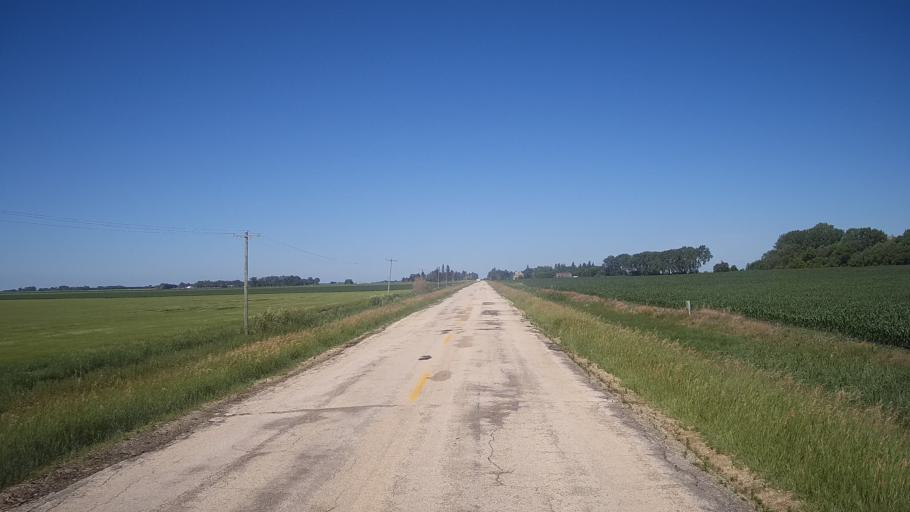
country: CA
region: Manitoba
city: Portage la Prairie
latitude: 50.0437
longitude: -98.0434
